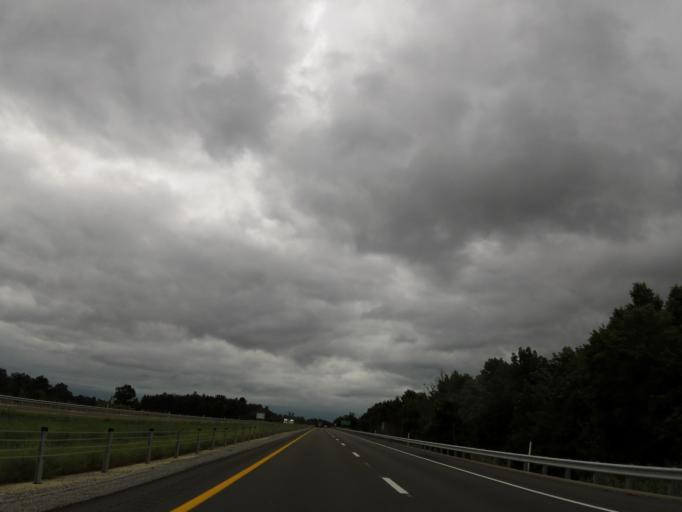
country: US
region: Illinois
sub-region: Massac County
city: Metropolis
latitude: 37.1046
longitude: -88.6904
